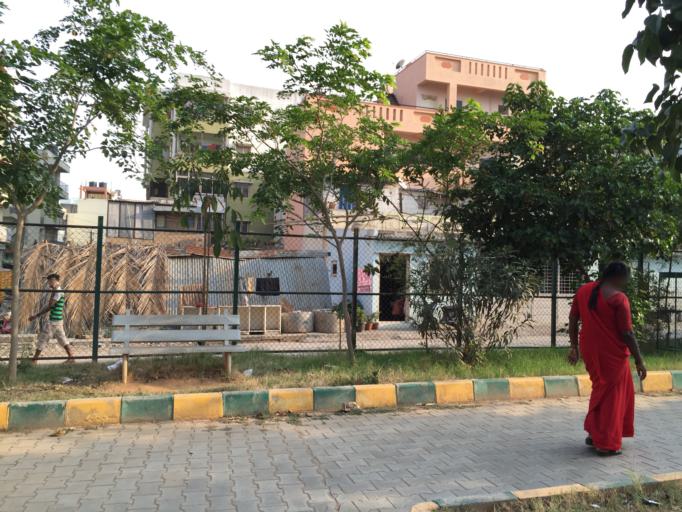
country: IN
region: Karnataka
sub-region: Bangalore Urban
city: Bangalore
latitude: 12.9027
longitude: 77.5759
